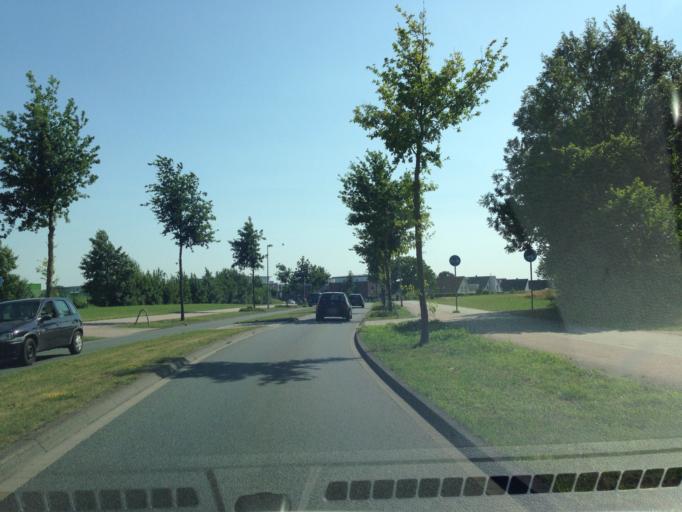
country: DE
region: North Rhine-Westphalia
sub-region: Regierungsbezirk Munster
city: Muenster
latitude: 51.9640
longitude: 7.5672
